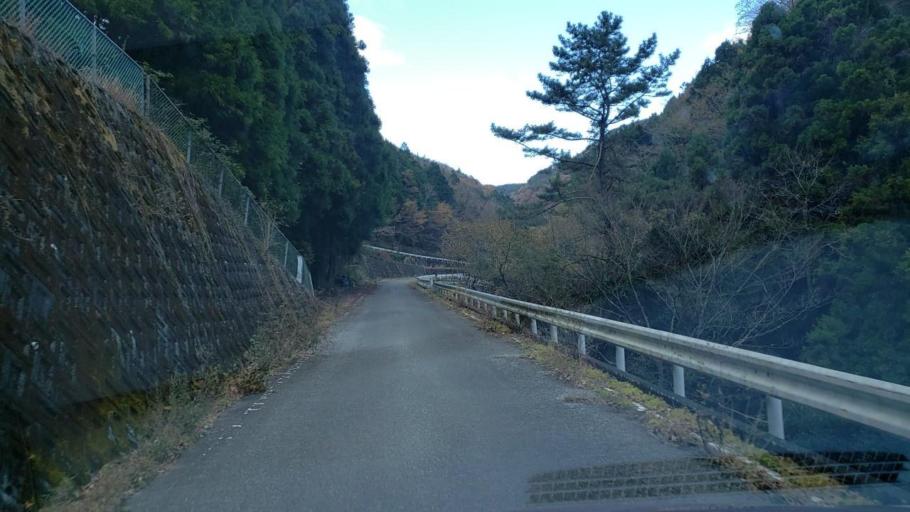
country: JP
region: Tokushima
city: Wakimachi
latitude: 34.1469
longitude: 134.2278
